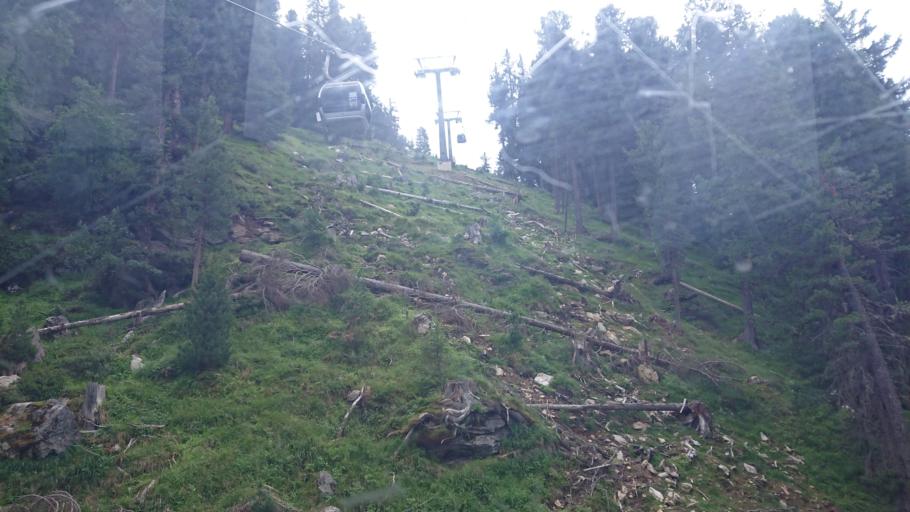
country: AT
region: Tyrol
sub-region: Politischer Bezirk Imst
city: Oetz
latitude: 47.2195
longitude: 10.9323
